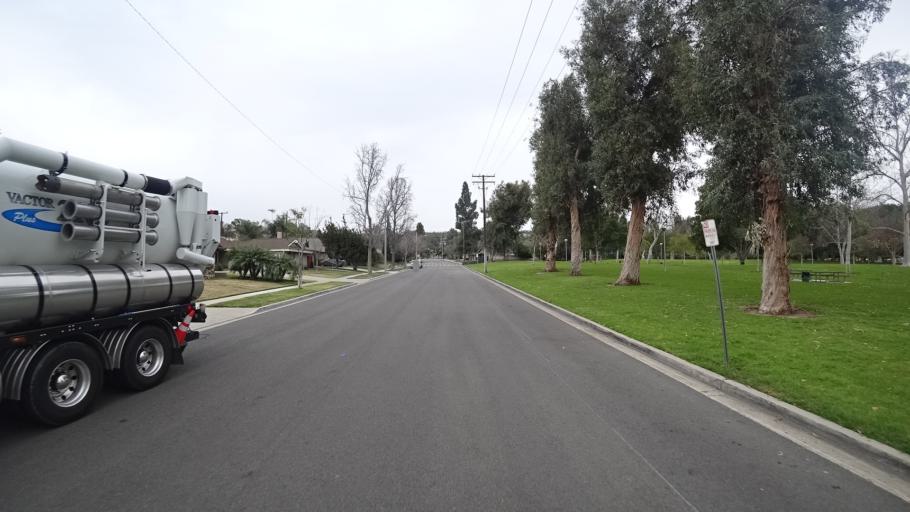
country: US
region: California
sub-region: Orange County
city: Yorba Linda
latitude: 33.8531
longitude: -117.8023
